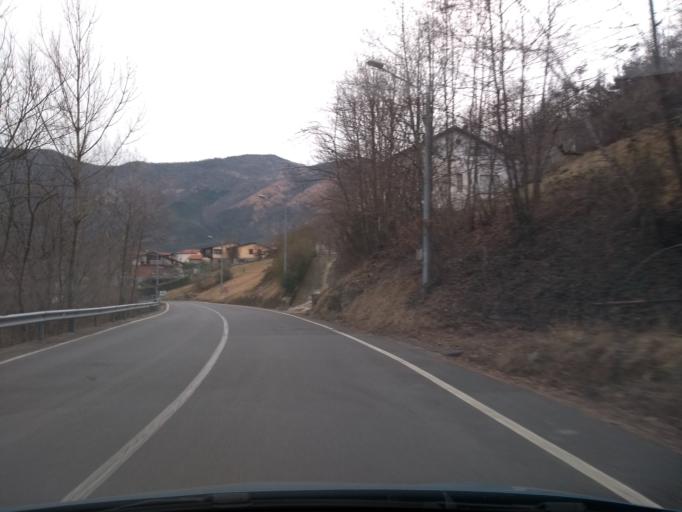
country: IT
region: Piedmont
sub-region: Provincia di Torino
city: La Villa
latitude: 45.2673
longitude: 7.4501
